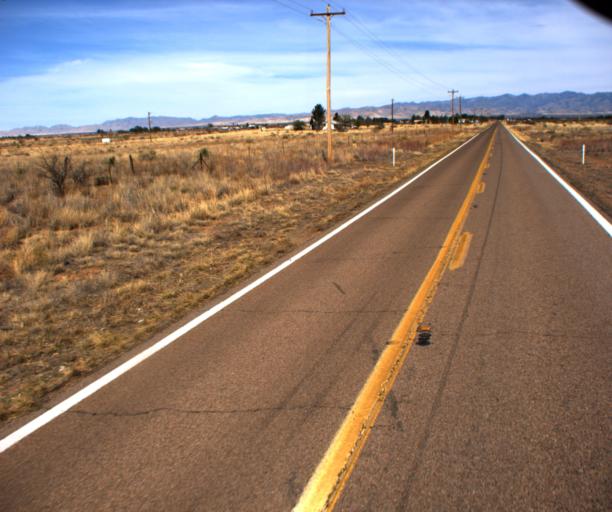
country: US
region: Arizona
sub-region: Cochise County
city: Willcox
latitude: 31.8764
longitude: -109.6594
